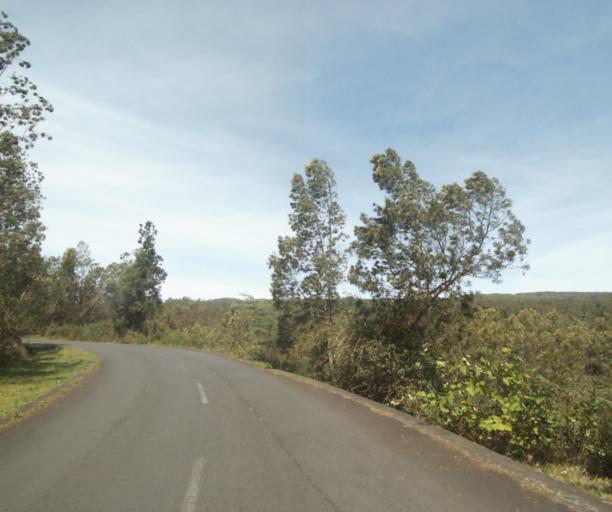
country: RE
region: Reunion
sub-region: Reunion
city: Trois-Bassins
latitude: -21.0492
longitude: 55.3422
